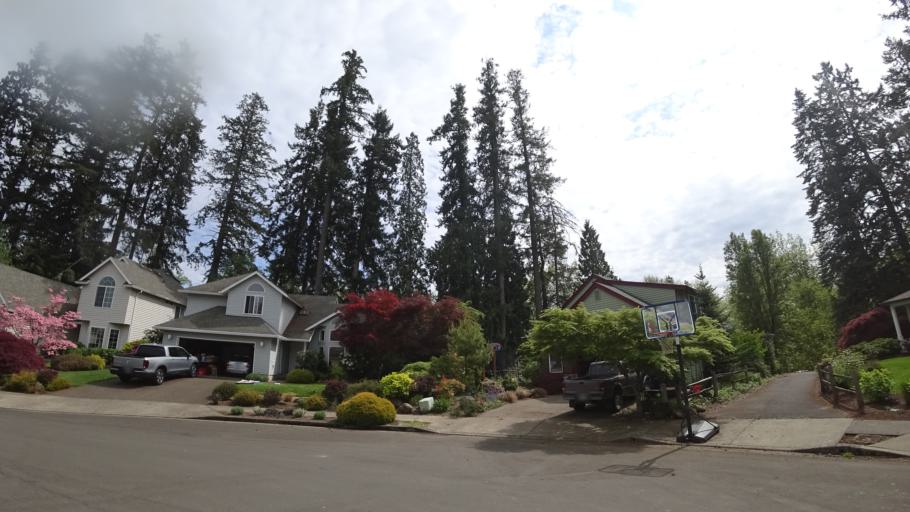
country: US
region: Oregon
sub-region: Washington County
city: Rockcreek
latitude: 45.5180
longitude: -122.9226
